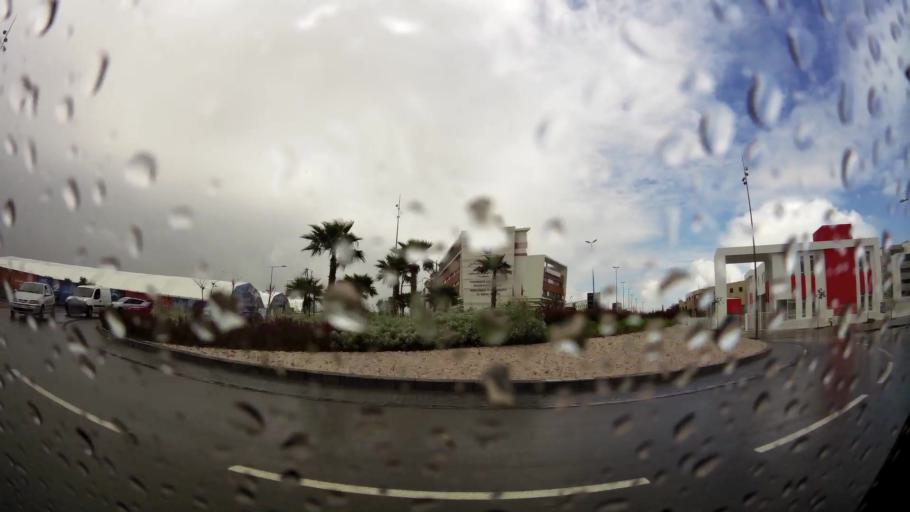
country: MA
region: Grand Casablanca
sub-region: Casablanca
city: Casablanca
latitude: 33.5529
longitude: -7.6650
